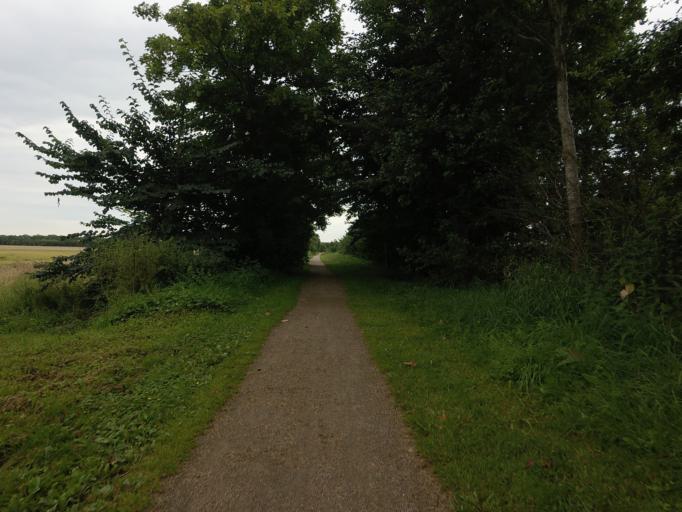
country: DK
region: North Denmark
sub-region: Alborg Kommune
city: Vadum
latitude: 57.1200
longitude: 9.8657
